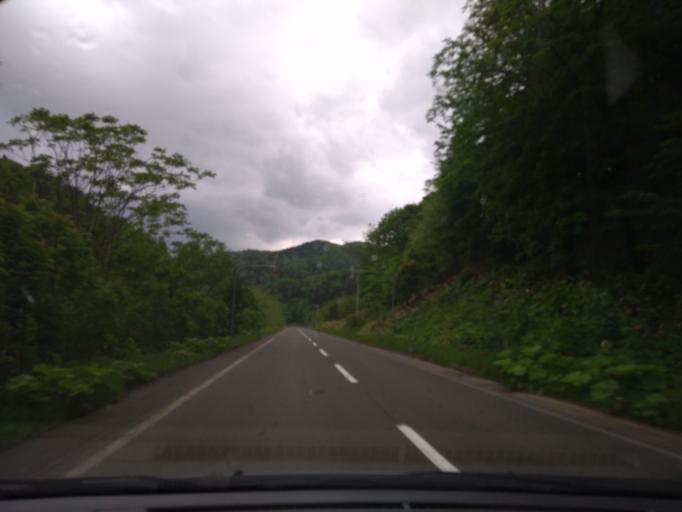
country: JP
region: Hokkaido
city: Shimo-furano
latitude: 43.1231
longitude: 142.4038
